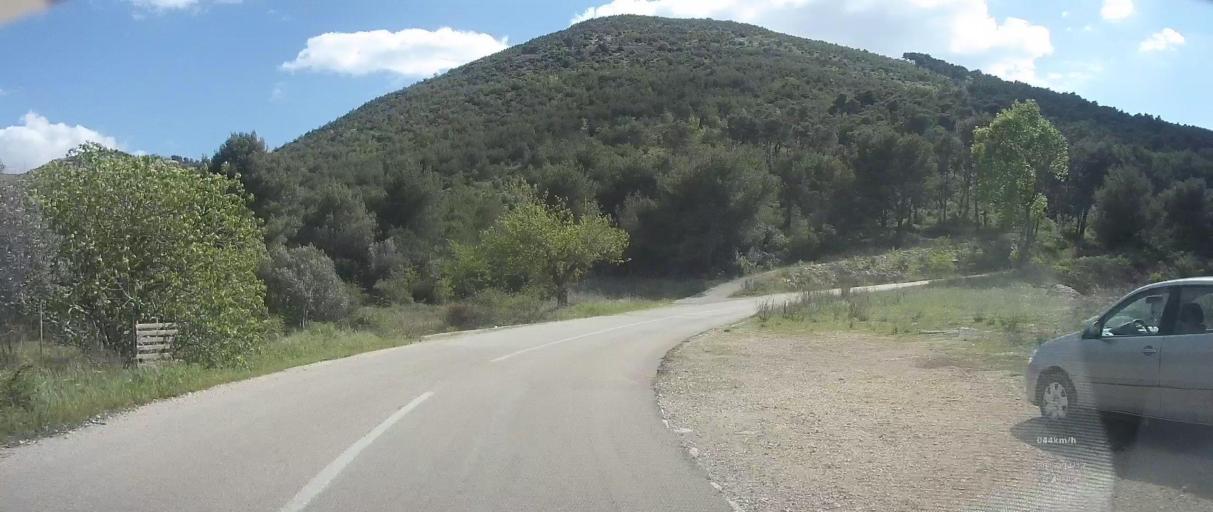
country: HR
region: Sibensko-Kniniska
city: Primosten
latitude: 43.6304
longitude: 15.9756
